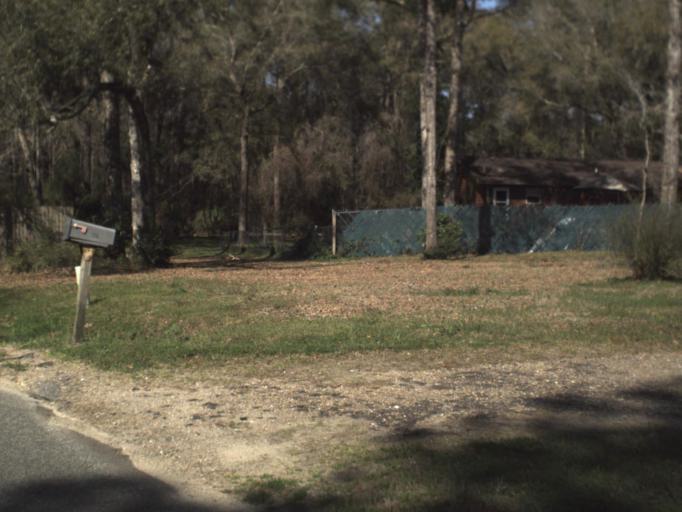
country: US
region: Florida
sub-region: Jackson County
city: Marianna
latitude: 30.6238
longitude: -85.1523
